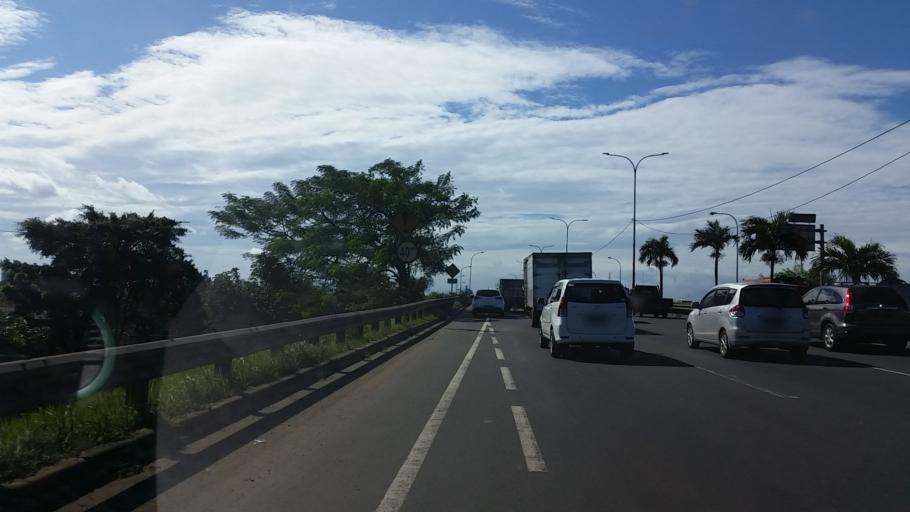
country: ID
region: Banten
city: South Tangerang
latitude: -6.2543
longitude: 106.7647
